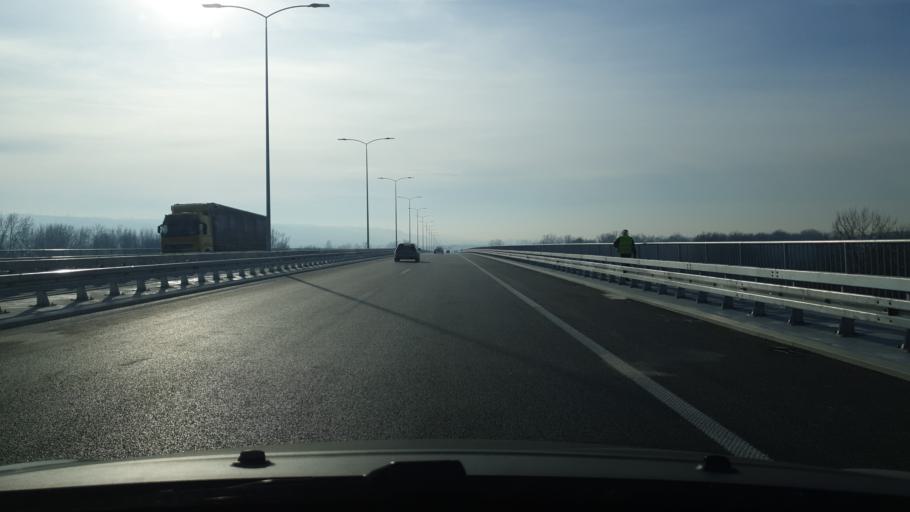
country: RS
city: Baric
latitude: 44.6646
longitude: 20.2445
